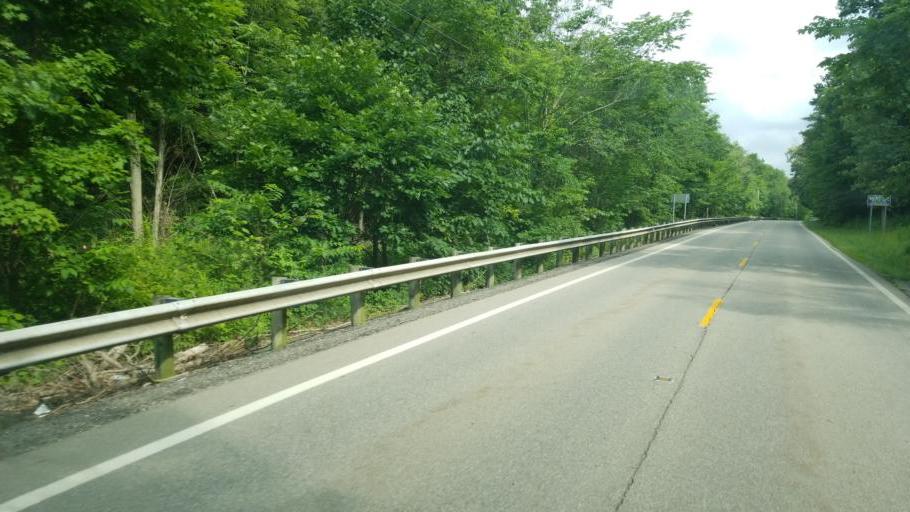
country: US
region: Ohio
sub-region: Columbiana County
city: Salineville
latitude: 40.6520
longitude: -80.8091
